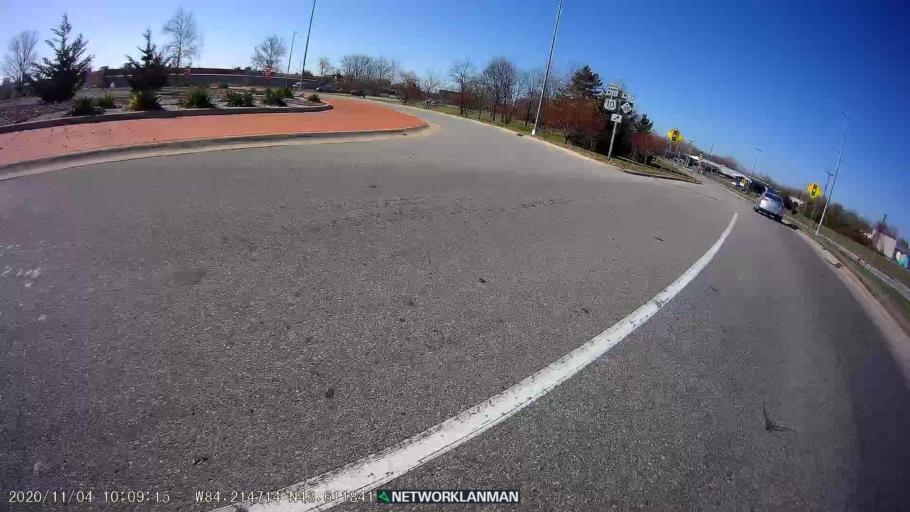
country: US
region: Michigan
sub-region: Midland County
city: Midland
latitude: 43.6119
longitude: -84.2150
